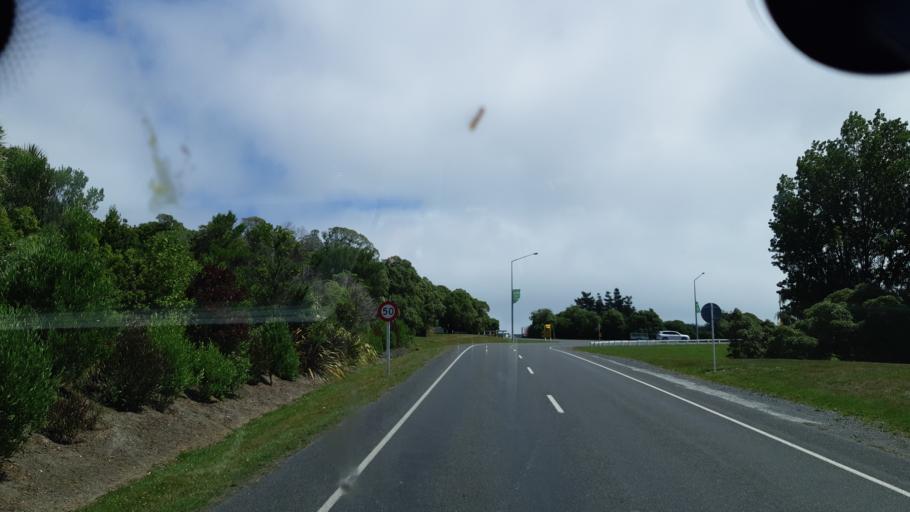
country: NZ
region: Canterbury
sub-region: Kaikoura District
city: Kaikoura
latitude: -42.4092
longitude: 173.6798
